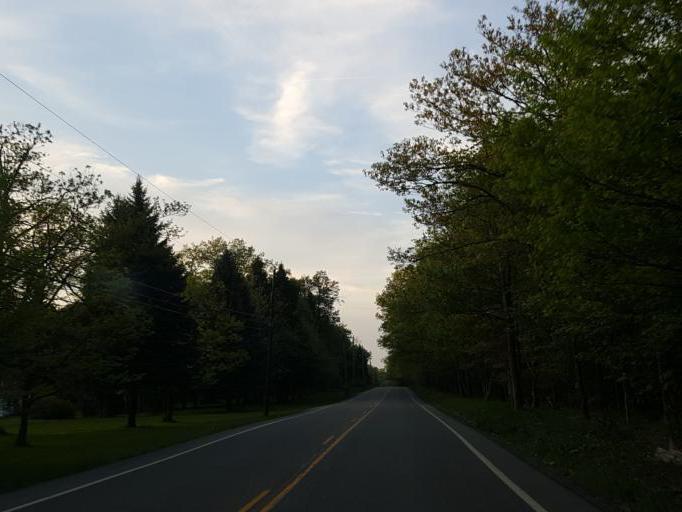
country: US
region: Pennsylvania
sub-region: Cambria County
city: Gallitzin
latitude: 40.5046
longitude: -78.5401
